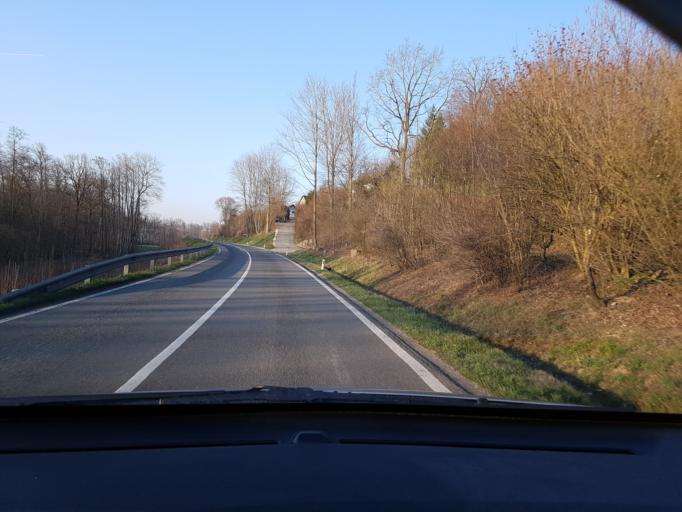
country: AT
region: Upper Austria
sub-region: Politischer Bezirk Linz-Land
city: Ansfelden
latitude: 48.1452
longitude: 14.3266
